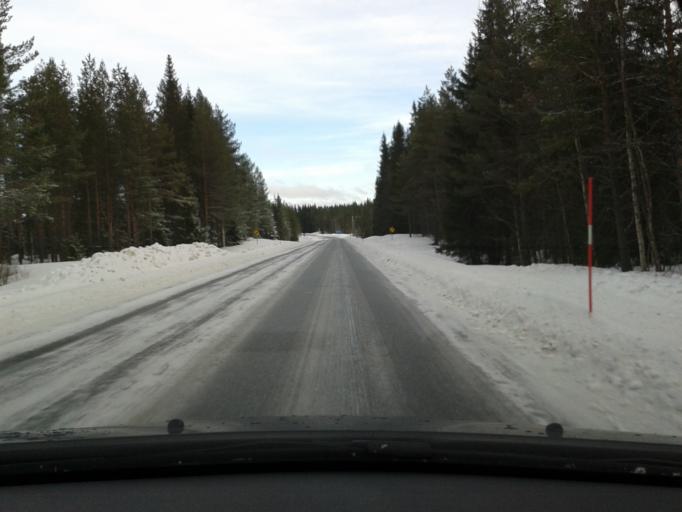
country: SE
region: Vaesterbotten
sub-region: Vilhelmina Kommun
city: Vilhelmina
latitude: 64.6441
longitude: 16.4967
